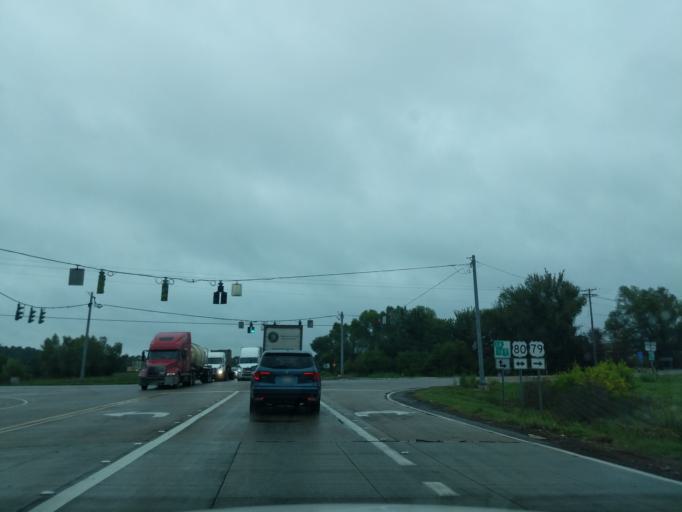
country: US
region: Louisiana
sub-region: Caddo Parish
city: Greenwood
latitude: 32.4430
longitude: -93.9817
